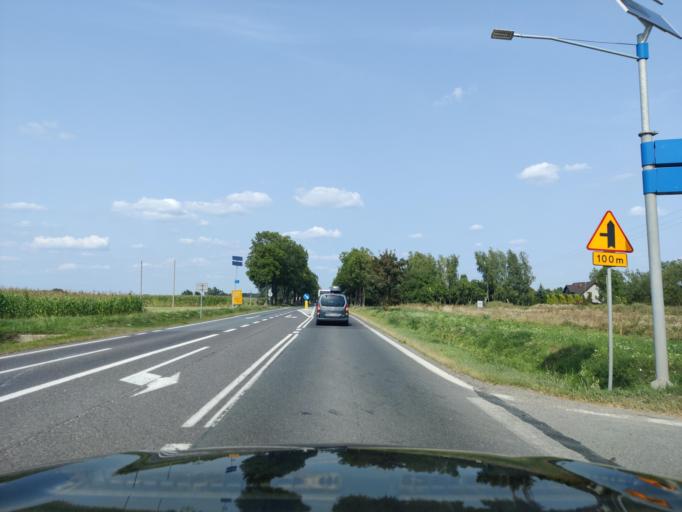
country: PL
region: Masovian Voivodeship
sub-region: Powiat pultuski
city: Pultusk
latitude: 52.7709
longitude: 21.1182
